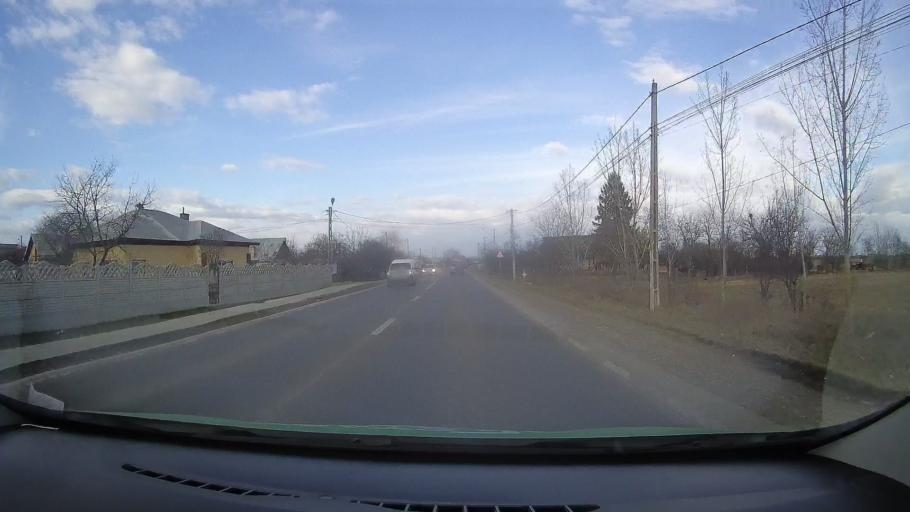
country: RO
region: Dambovita
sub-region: Comuna Ulmi
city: Viisoara
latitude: 44.8884
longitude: 25.4342
